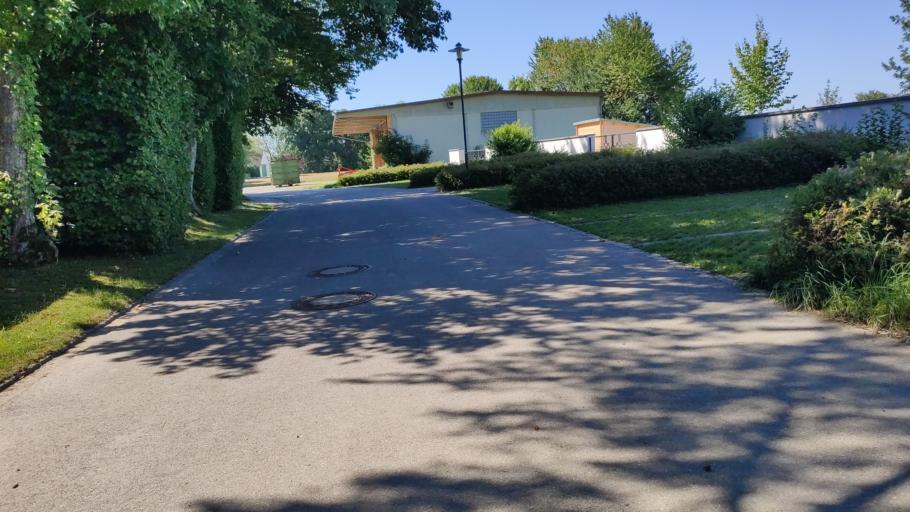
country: DE
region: Bavaria
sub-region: Swabia
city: Kleinaitingen
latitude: 48.2207
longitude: 10.8396
